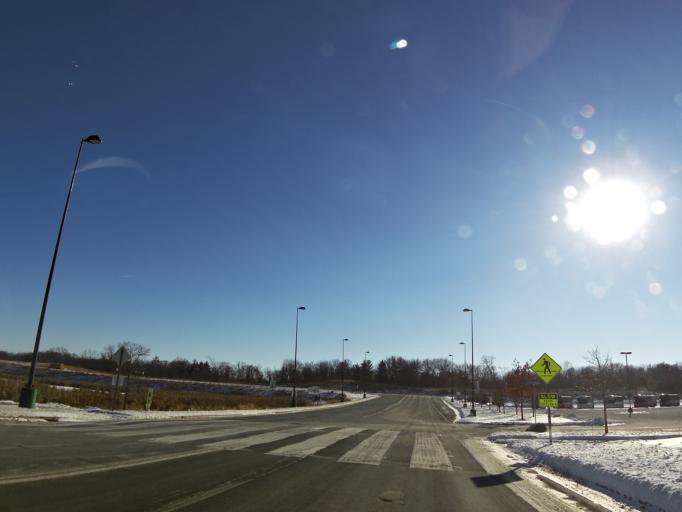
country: US
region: Minnesota
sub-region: Scott County
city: Prior Lake
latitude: 44.7253
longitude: -93.4750
